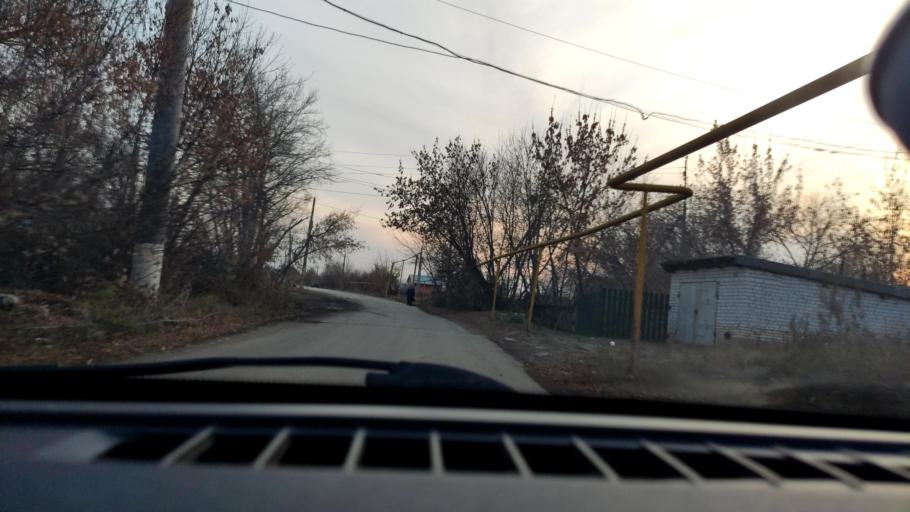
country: RU
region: Samara
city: Samara
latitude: 53.1482
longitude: 50.1357
